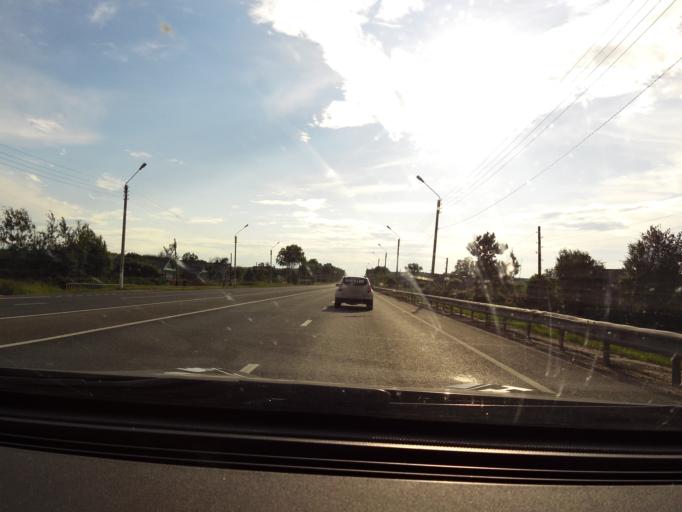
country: RU
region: Vladimir
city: Krasnyy Oktyabr'
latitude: 56.2194
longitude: 41.4823
